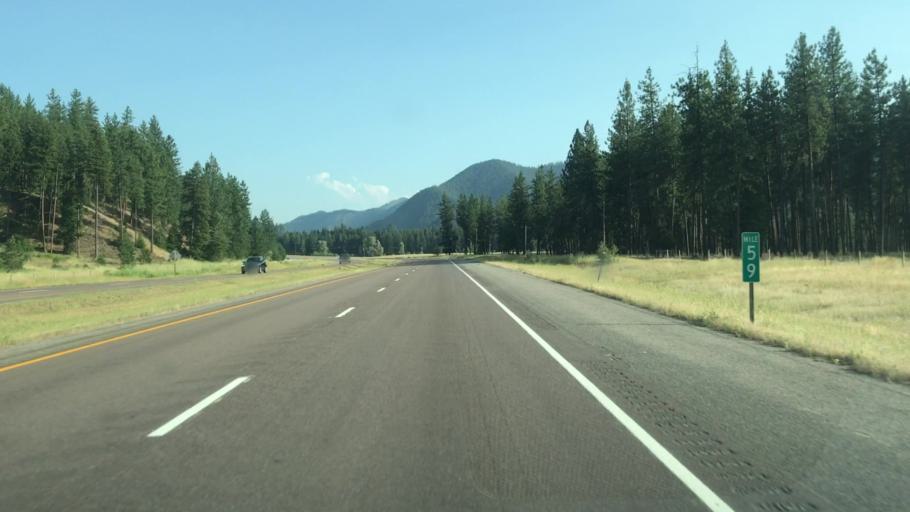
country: US
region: Montana
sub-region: Mineral County
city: Superior
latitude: 47.0621
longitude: -114.7636
